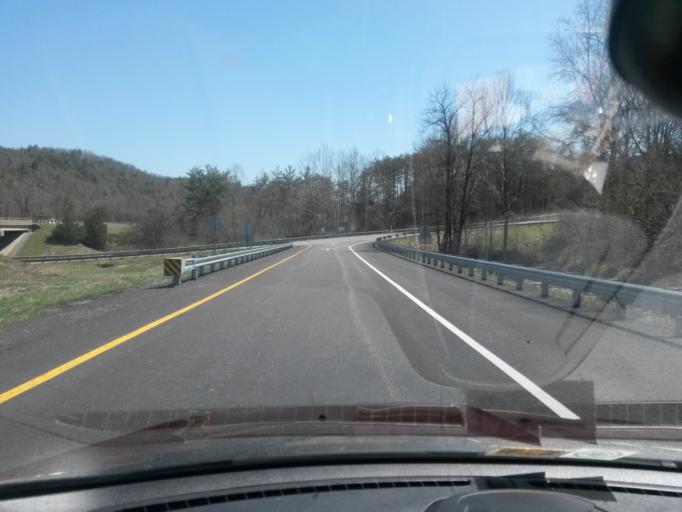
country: US
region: Virginia
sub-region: City of Covington
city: Covington
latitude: 37.8179
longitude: -80.1135
